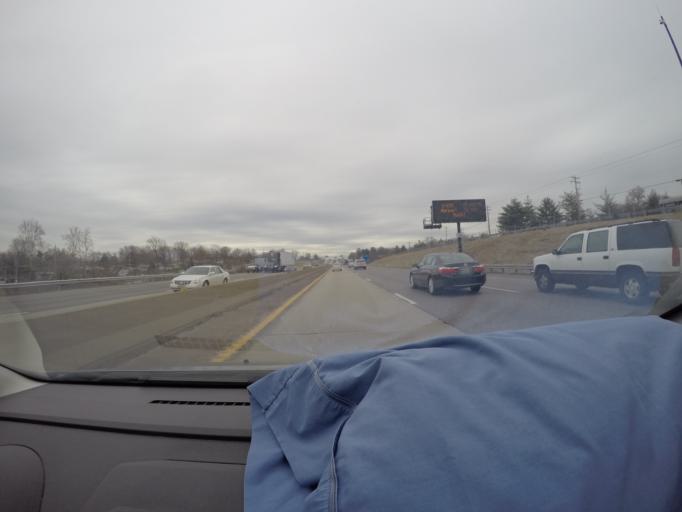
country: US
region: Missouri
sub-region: Saint Charles County
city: Saint Charles
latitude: 38.7898
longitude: -90.5496
